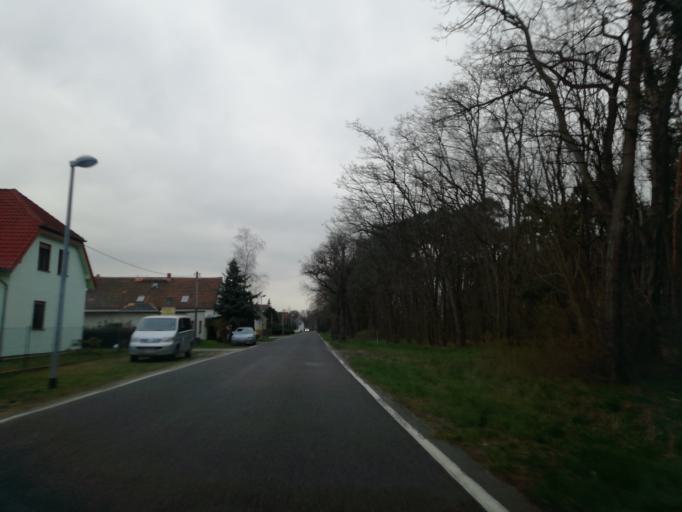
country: DE
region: Brandenburg
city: Vetschau
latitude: 51.7652
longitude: 14.1316
